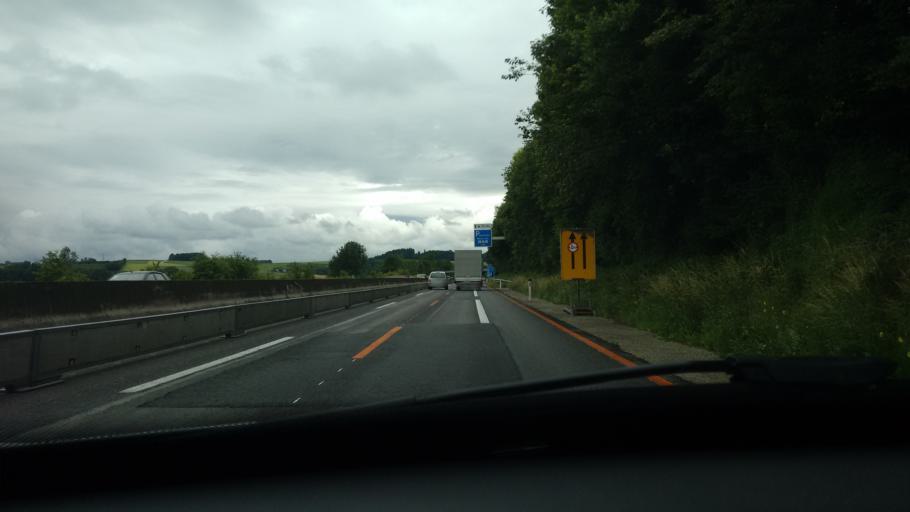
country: AT
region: Upper Austria
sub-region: Wels Stadt
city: Wels
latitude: 48.1784
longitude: 13.9853
